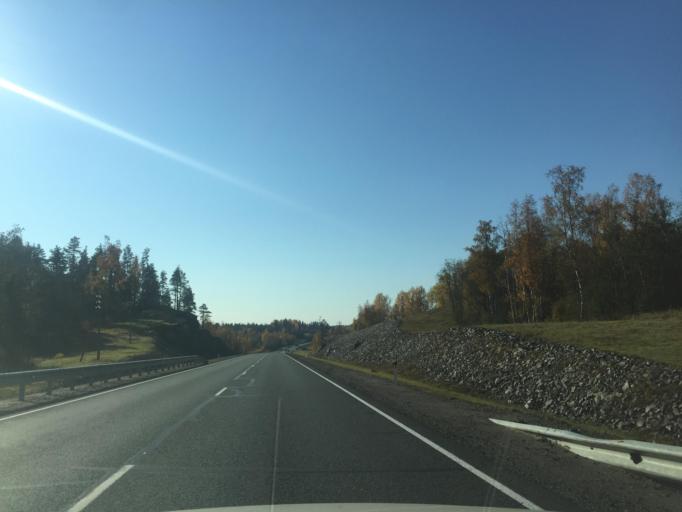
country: RU
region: Leningrad
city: Kuznechnoye
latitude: 61.3525
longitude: 29.8837
